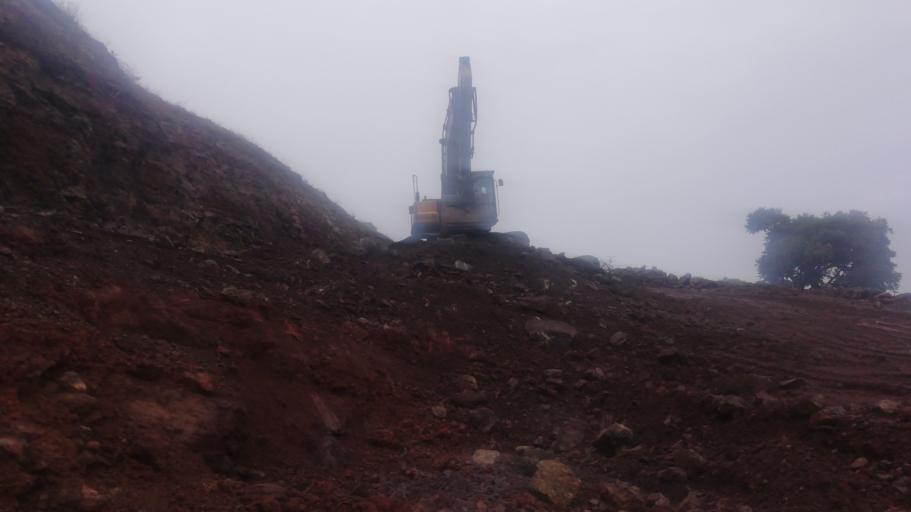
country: ET
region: Amhara
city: Addiet Canna
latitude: 11.2298
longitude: 37.8881
